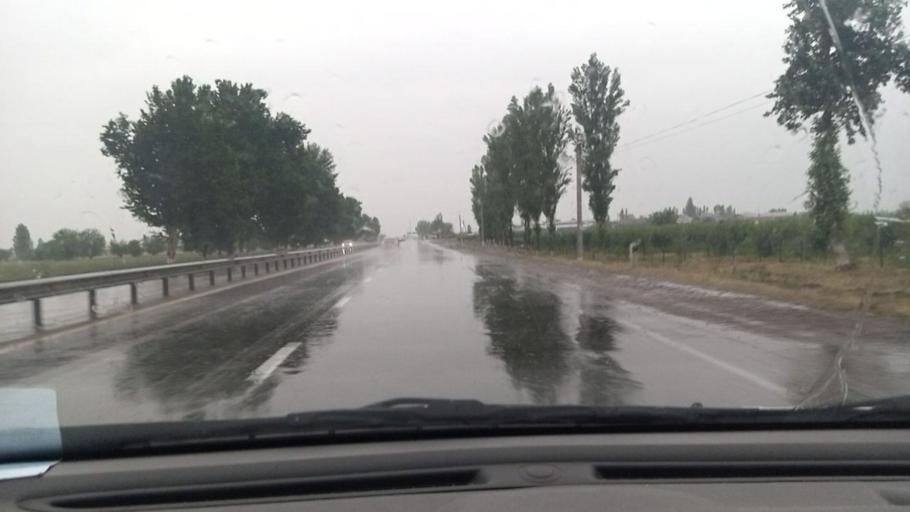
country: UZ
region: Toshkent Shahri
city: Bektemir
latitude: 41.1405
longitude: 69.4331
